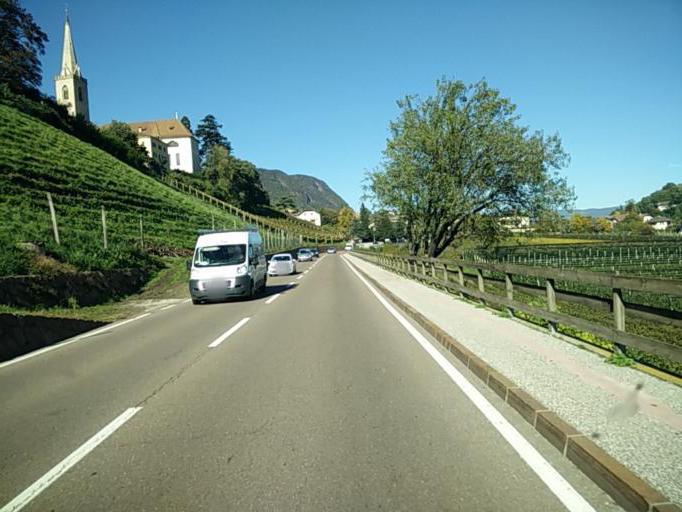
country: IT
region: Trentino-Alto Adige
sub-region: Bolzano
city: Caldaro sulla Strada del Vino
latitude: 46.4115
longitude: 11.2480
